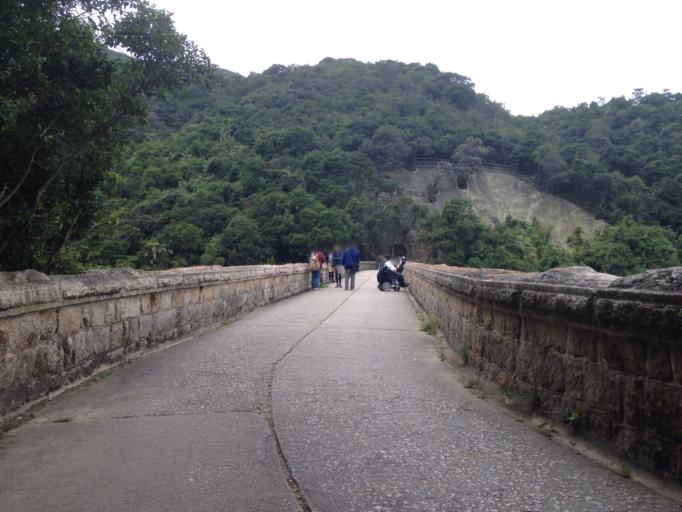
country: HK
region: Wanchai
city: Wan Chai
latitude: 22.2411
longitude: 114.2182
